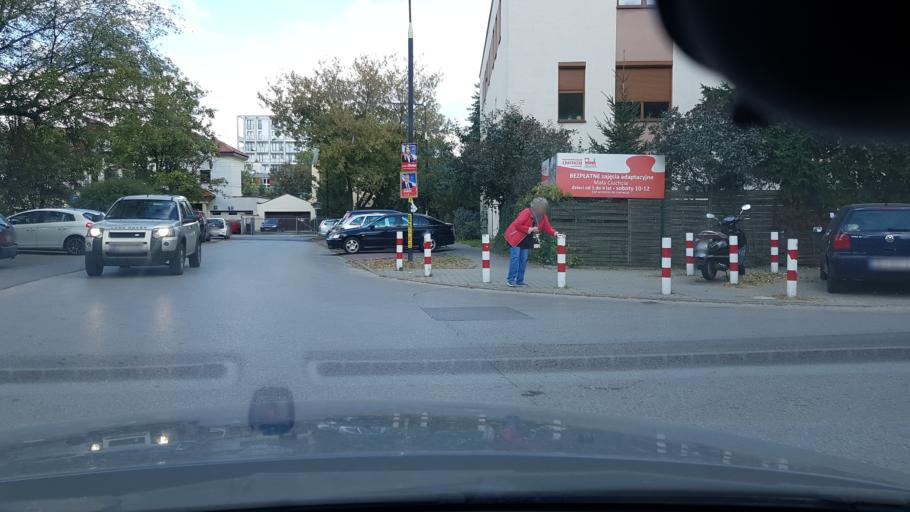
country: PL
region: Masovian Voivodeship
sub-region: Warszawa
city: Bielany
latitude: 52.2745
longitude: 20.9309
